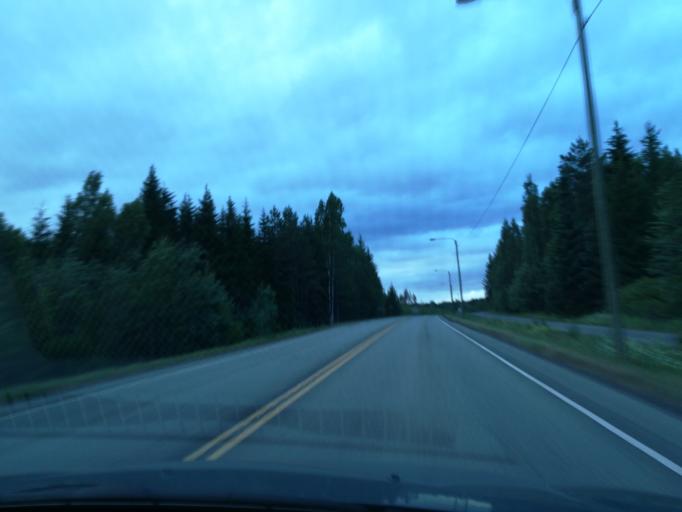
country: FI
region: Southern Savonia
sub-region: Mikkeli
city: Ristiina
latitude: 61.5020
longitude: 27.2379
